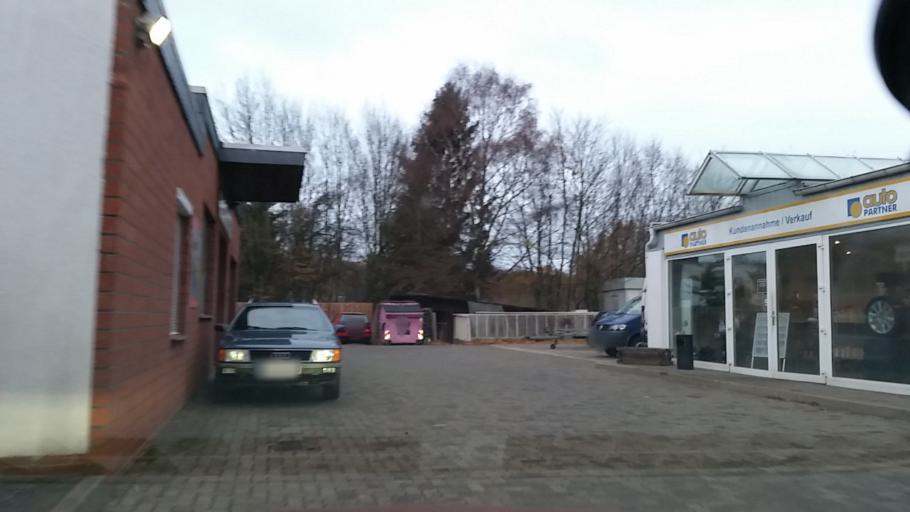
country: DE
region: Lower Saxony
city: Wittingen
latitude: 52.7318
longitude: 10.7363
